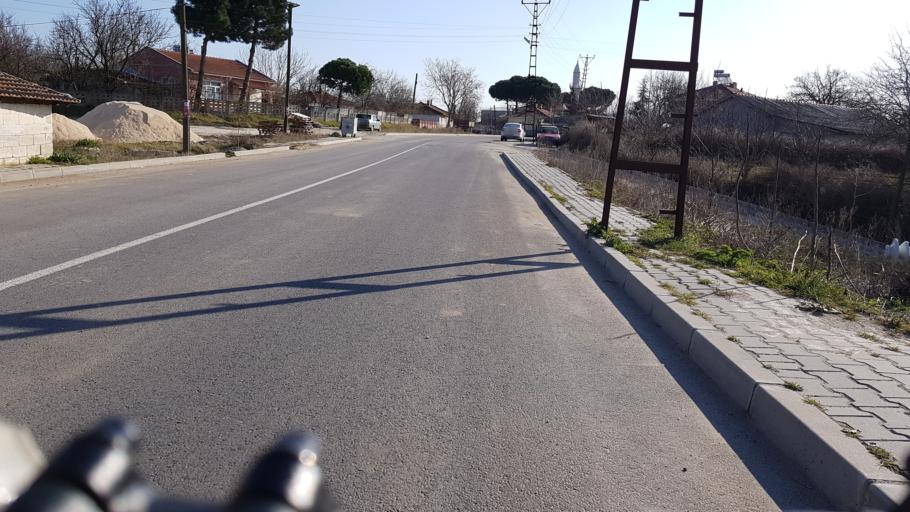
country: TR
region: Tekirdag
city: Velimese
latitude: 41.3463
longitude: 27.8360
